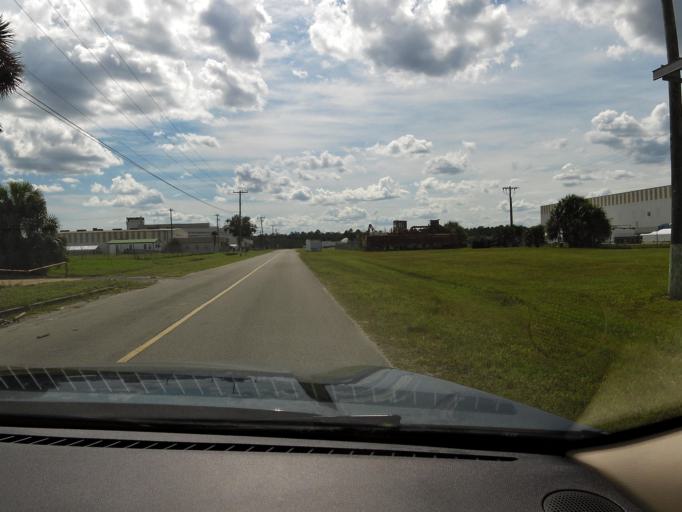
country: US
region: Florida
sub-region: Clay County
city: Green Cove Springs
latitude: 29.9779
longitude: -81.6569
